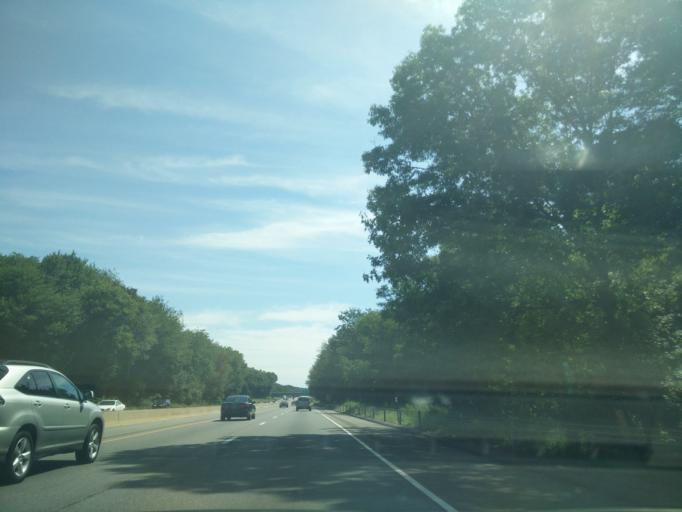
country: US
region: Connecticut
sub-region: New Haven County
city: Madison Center
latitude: 41.2883
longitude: -72.6328
